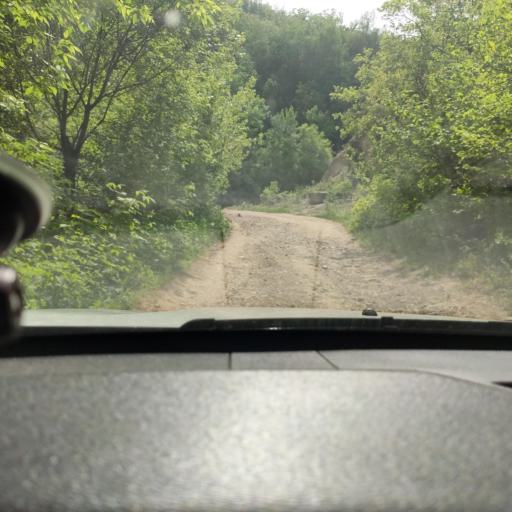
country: RU
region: Samara
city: Volzhskiy
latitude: 53.3377
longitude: 50.2088
